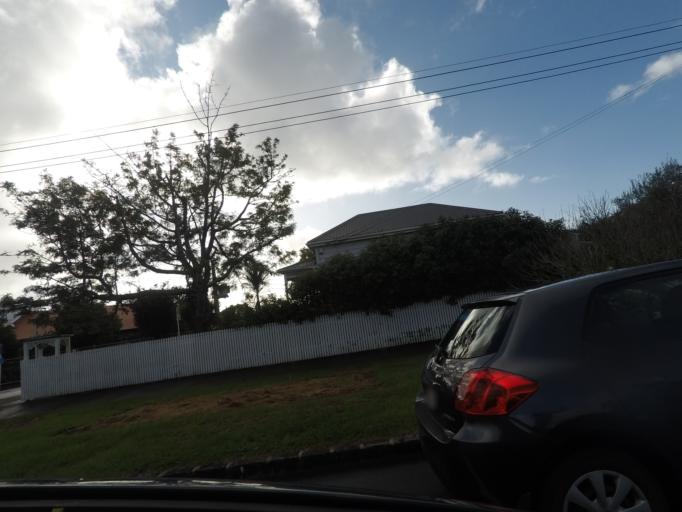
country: NZ
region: Auckland
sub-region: Auckland
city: Auckland
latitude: -36.8568
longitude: 174.7401
